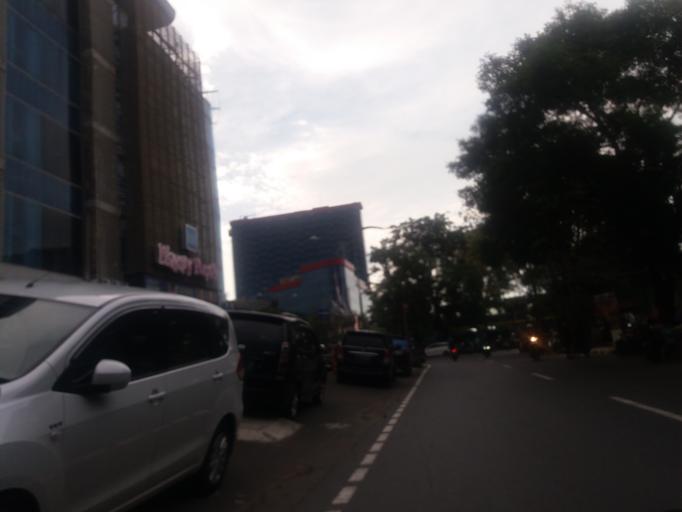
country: ID
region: Jakarta Raya
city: Jakarta
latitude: -6.1497
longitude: 106.8345
